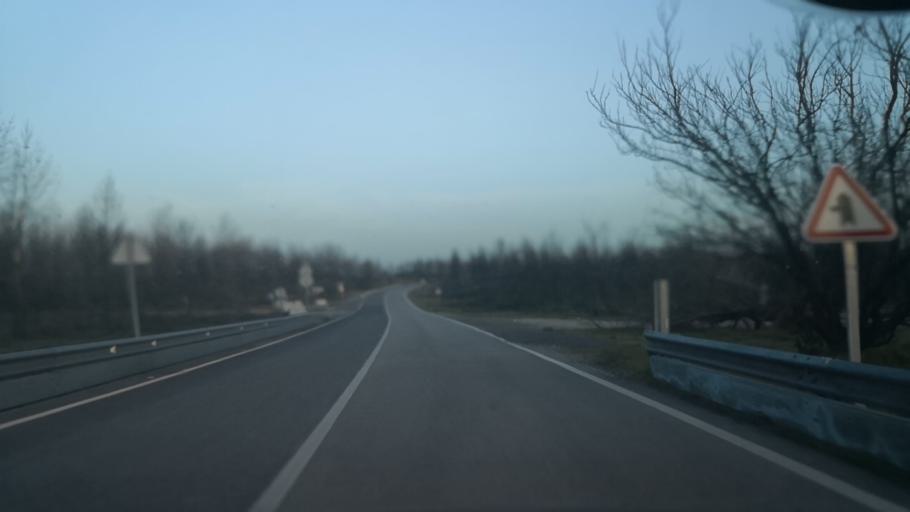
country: PT
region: Leiria
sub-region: Marinha Grande
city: Marinha Grande
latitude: 39.7468
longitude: -8.9749
